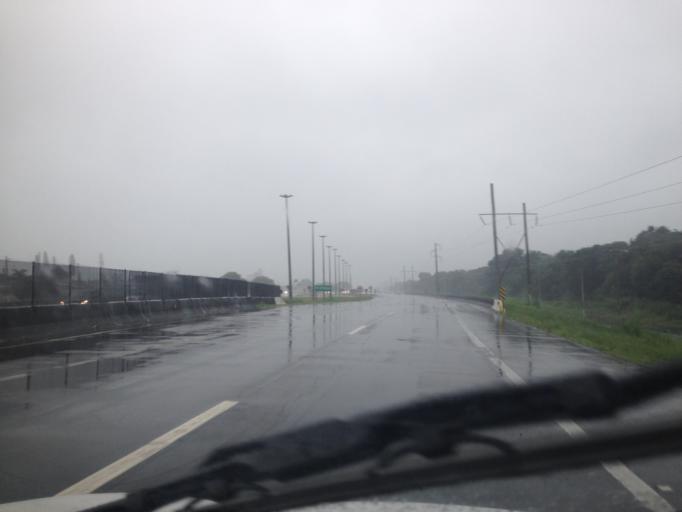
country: BR
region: Sao Paulo
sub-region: Mongagua
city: Mongagua
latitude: -24.0650
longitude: -46.5687
